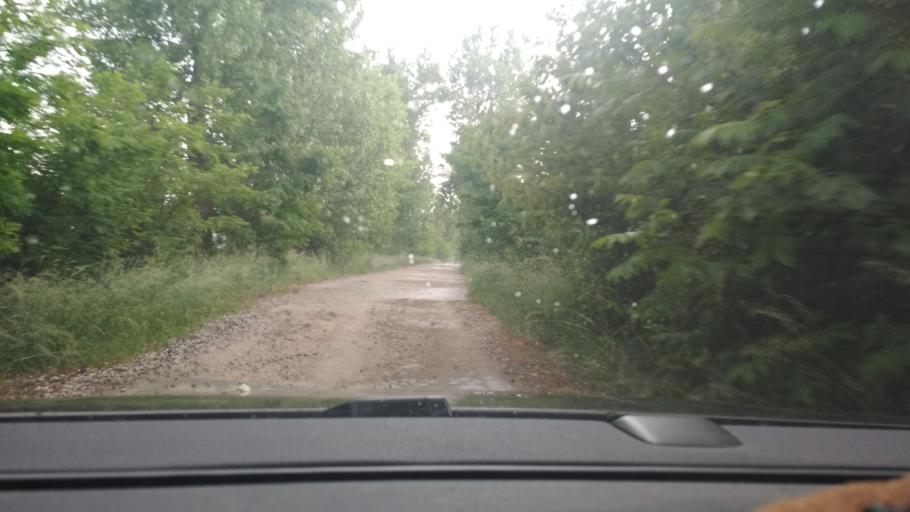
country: MD
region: Singerei
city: Biruinta
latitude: 47.7479
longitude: 28.1397
